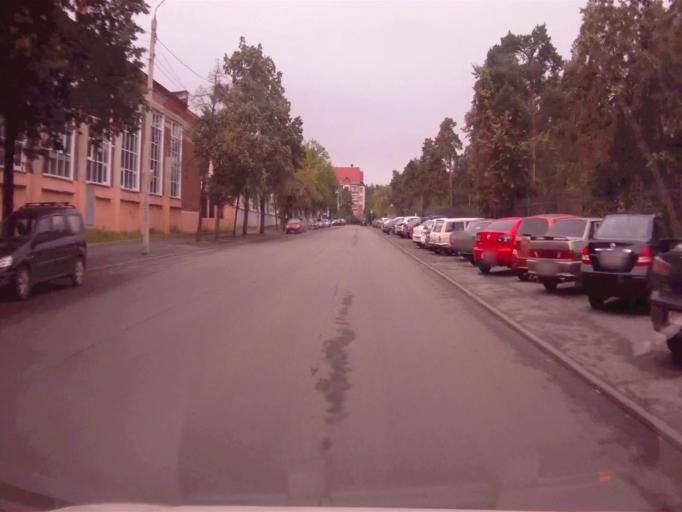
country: RU
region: Chelyabinsk
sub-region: Gorod Chelyabinsk
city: Chelyabinsk
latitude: 55.1614
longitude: 61.3680
